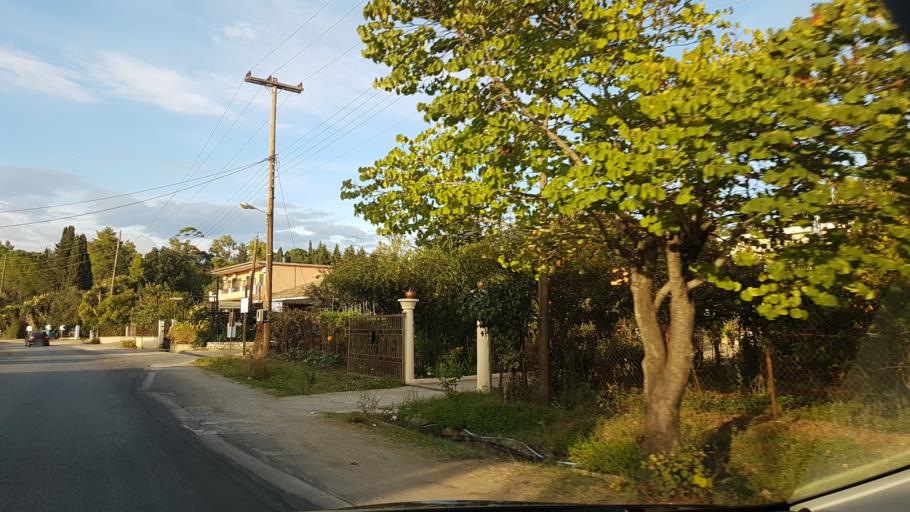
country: GR
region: Ionian Islands
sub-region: Nomos Kerkyras
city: Kontokali
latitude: 39.6665
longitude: 19.8434
